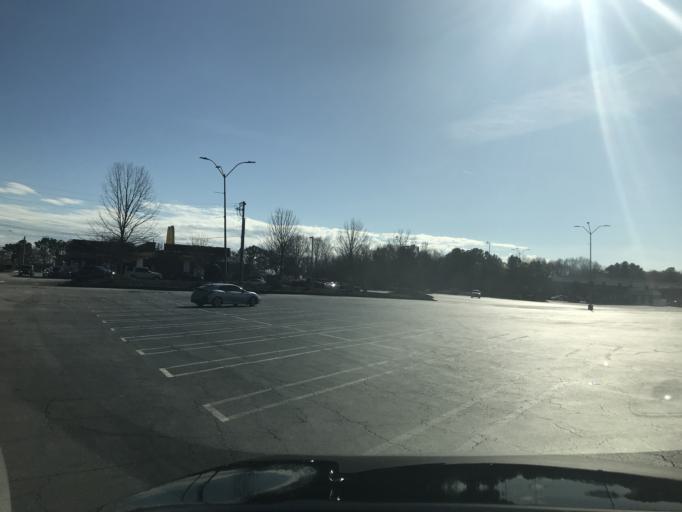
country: US
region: Georgia
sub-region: Coweta County
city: Newnan
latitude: 33.3858
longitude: -84.7852
